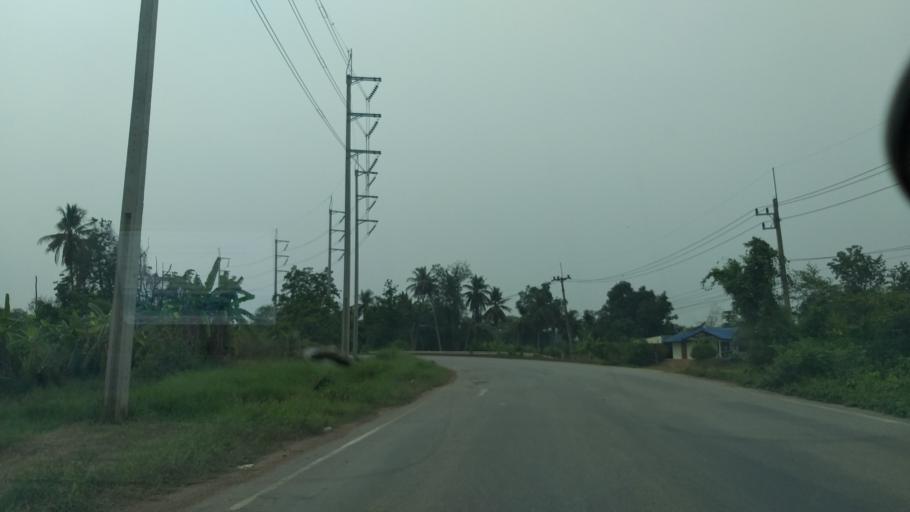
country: TH
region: Chachoengsao
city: Plaeng Yao
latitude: 13.5718
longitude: 101.2617
